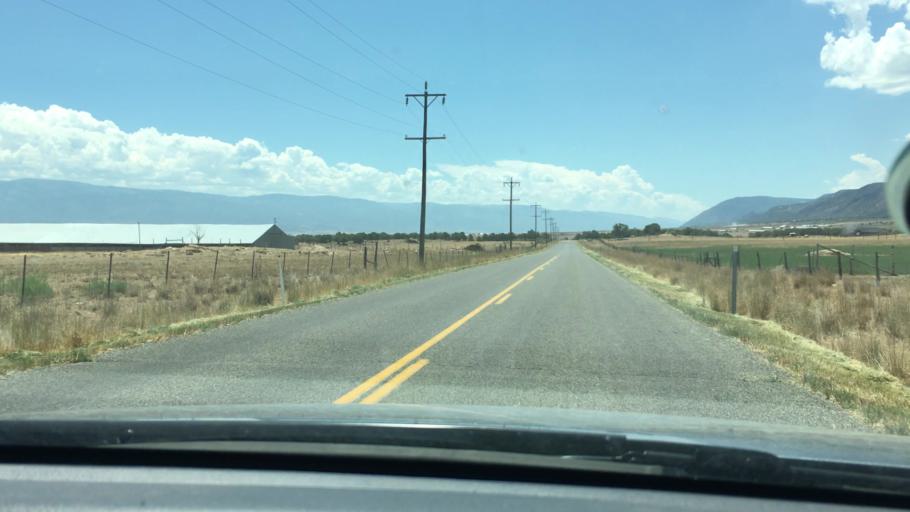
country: US
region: Utah
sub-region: Sanpete County
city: Fountain Green
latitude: 39.5975
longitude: -111.6433
